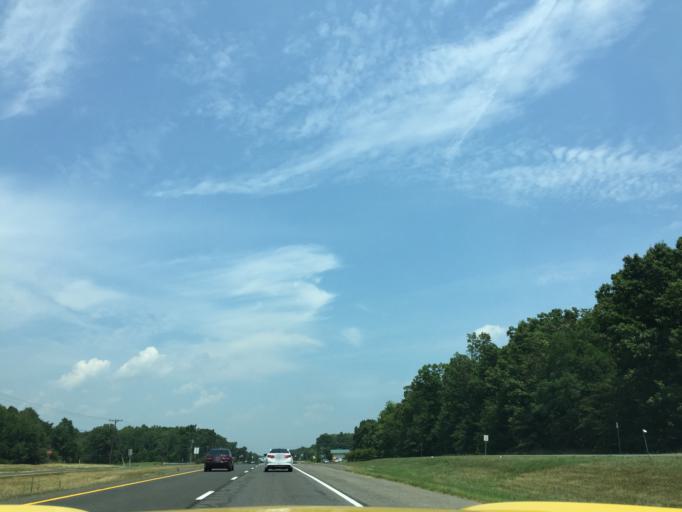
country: US
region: Maryland
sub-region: Prince George's County
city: Accokeek
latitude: 38.6479
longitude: -77.0378
